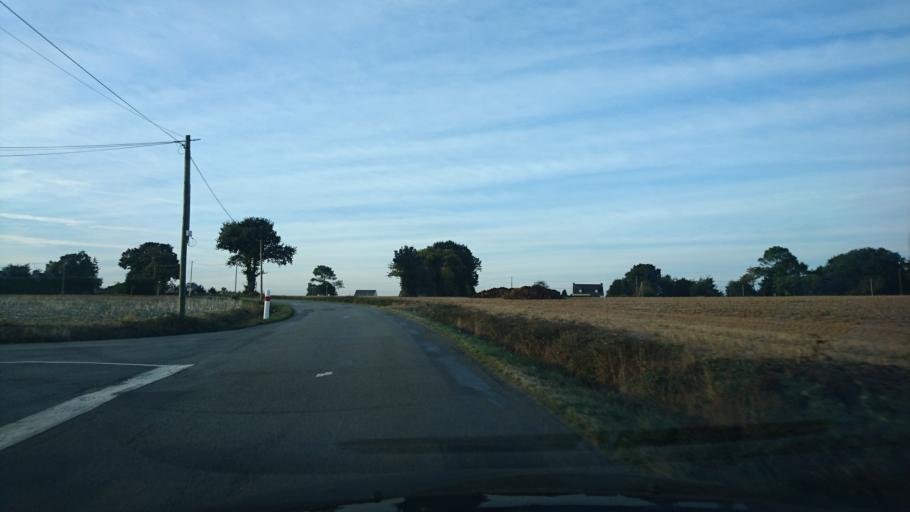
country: FR
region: Brittany
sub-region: Departement d'Ille-et-Vilaine
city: Sixt-sur-Aff
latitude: 47.7605
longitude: -2.0632
